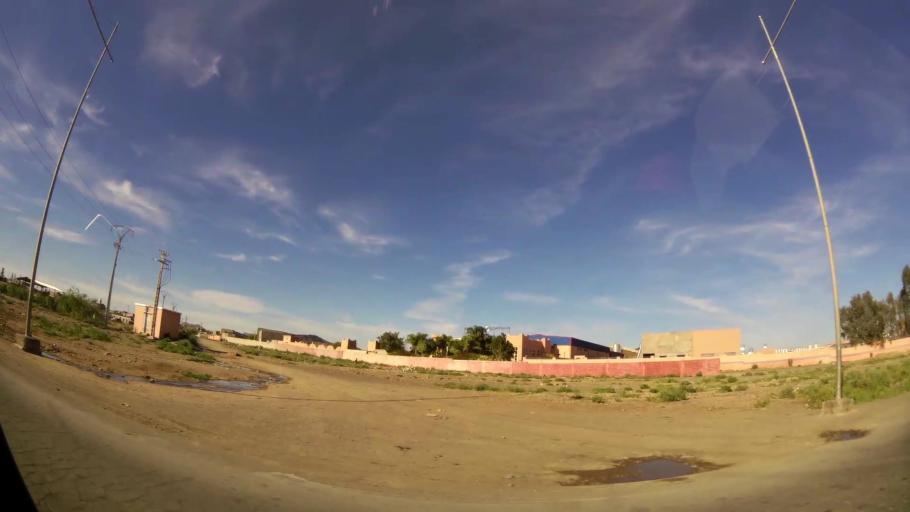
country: MA
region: Marrakech-Tensift-Al Haouz
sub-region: Marrakech
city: Marrakesh
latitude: 31.7135
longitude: -8.0733
